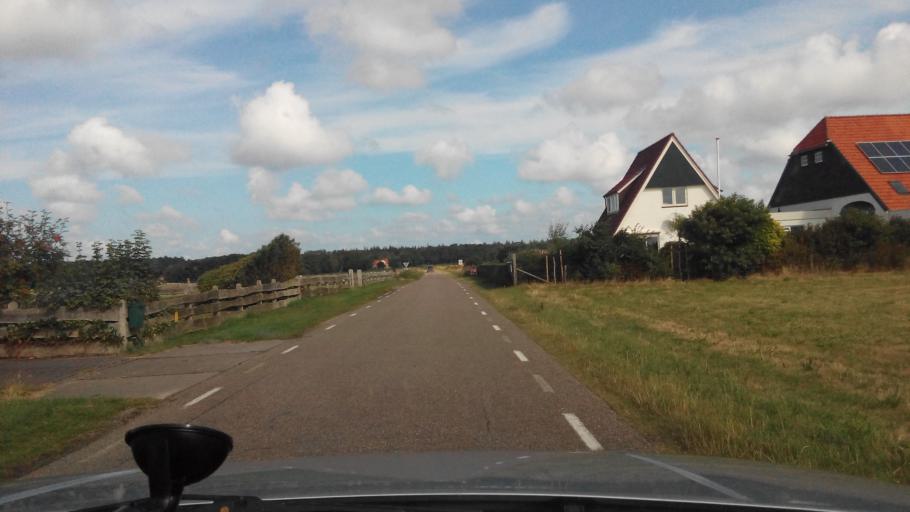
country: NL
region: North Holland
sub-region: Gemeente Texel
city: Den Burg
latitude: 53.0475
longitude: 4.7550
